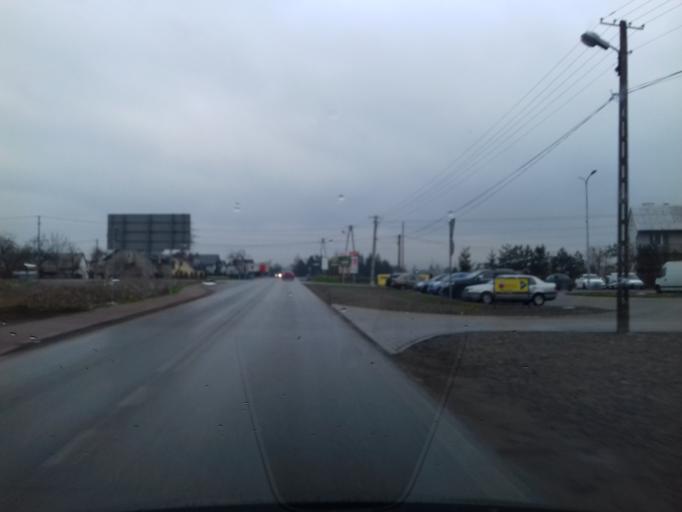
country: PL
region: Lesser Poland Voivodeship
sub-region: Powiat nowosadecki
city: Stary Sacz
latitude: 49.5924
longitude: 20.6298
